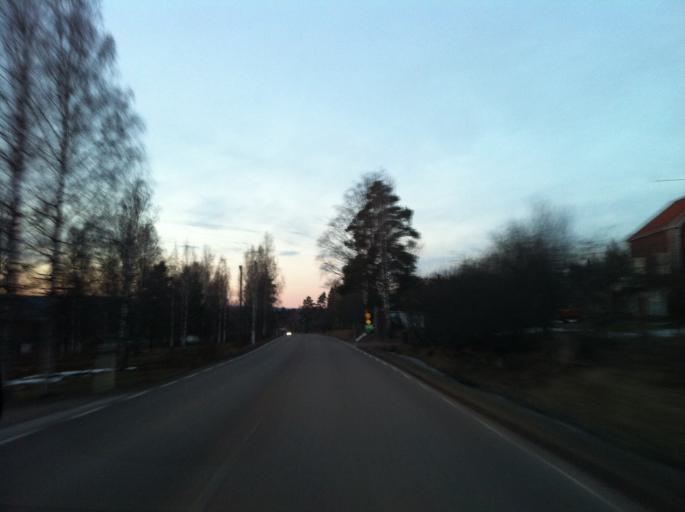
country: SE
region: Dalarna
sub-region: Orsa Kommun
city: Orsa
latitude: 61.0956
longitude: 14.6351
